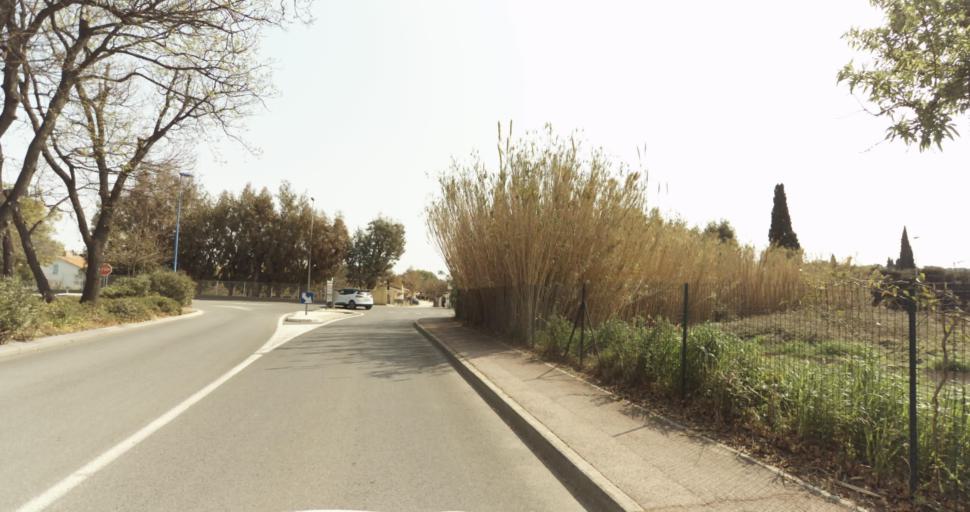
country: FR
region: Provence-Alpes-Cote d'Azur
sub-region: Departement du Var
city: Bormes-les-Mimosas
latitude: 43.1352
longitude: 6.3508
